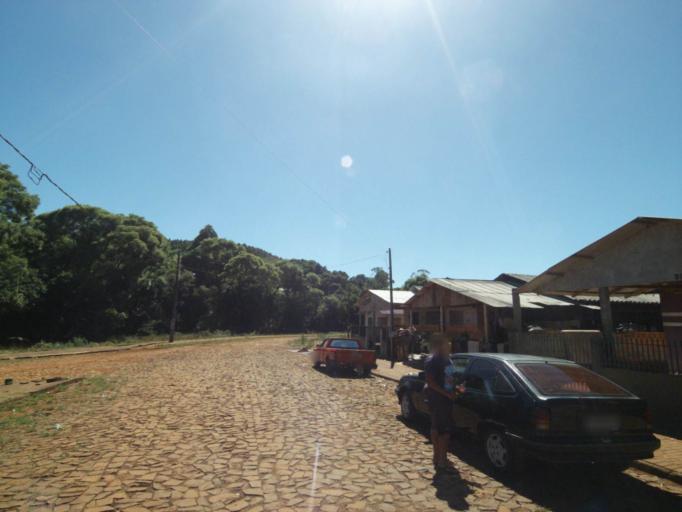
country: BR
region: Santa Catarina
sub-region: Sao Lourenco Do Oeste
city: Sao Lourenco dOeste
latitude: -26.2719
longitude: -52.7767
